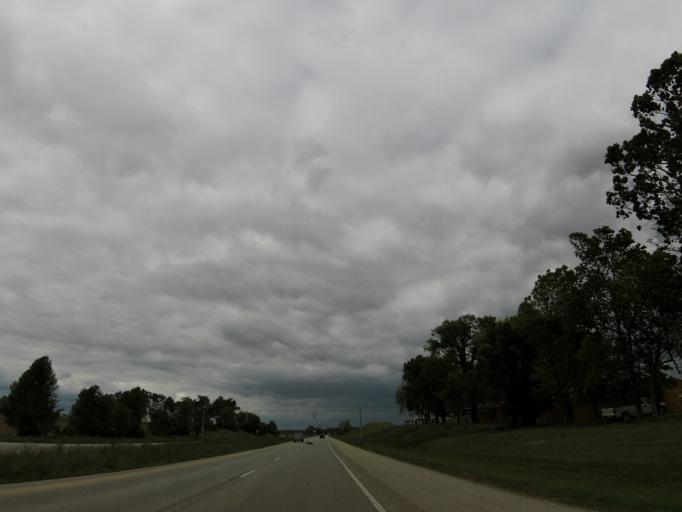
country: US
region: Kentucky
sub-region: Scott County
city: Georgetown
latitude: 38.1923
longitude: -84.5416
